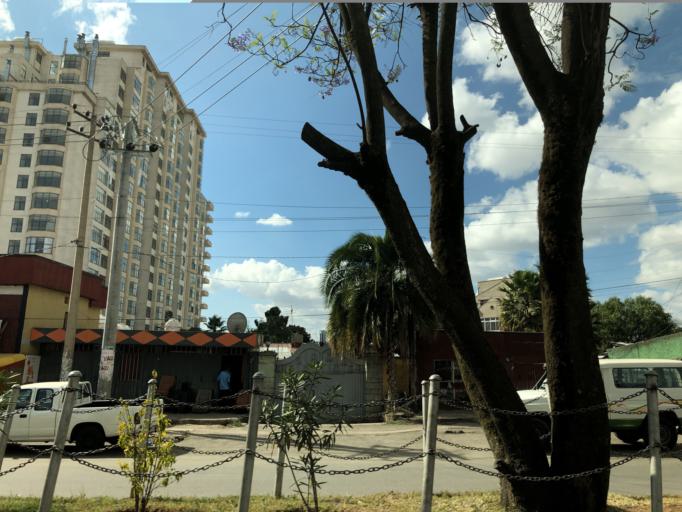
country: ET
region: Adis Abeba
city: Addis Ababa
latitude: 9.0055
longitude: 38.7809
